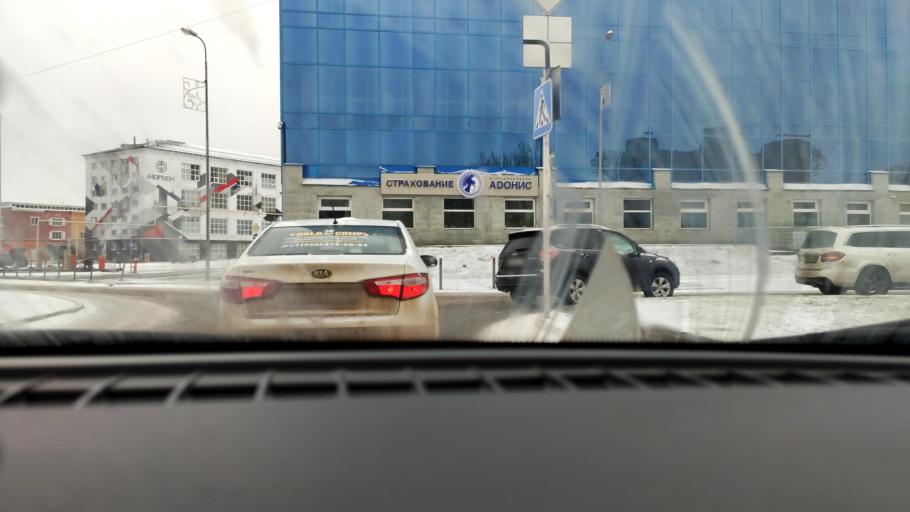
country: RU
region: Perm
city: Perm
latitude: 57.9924
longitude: 56.2041
